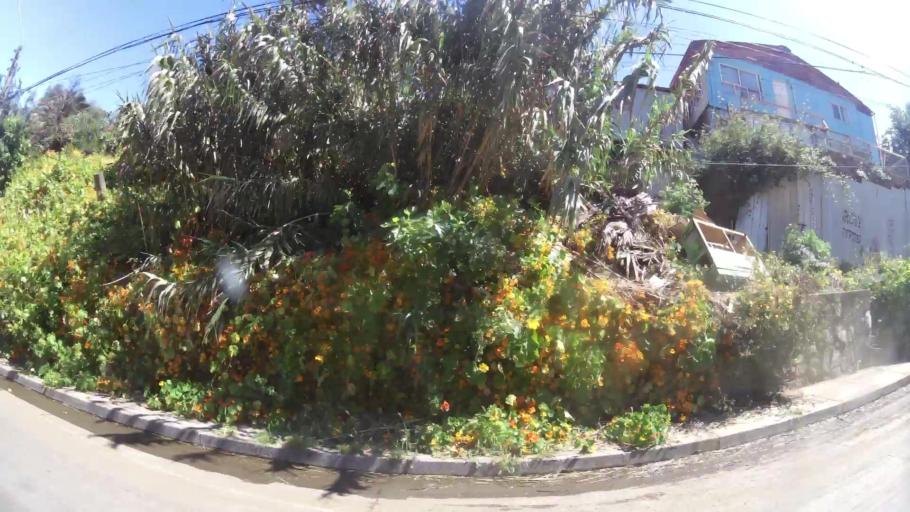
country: CL
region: Valparaiso
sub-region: Provincia de Valparaiso
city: Valparaiso
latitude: -33.0482
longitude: -71.5967
